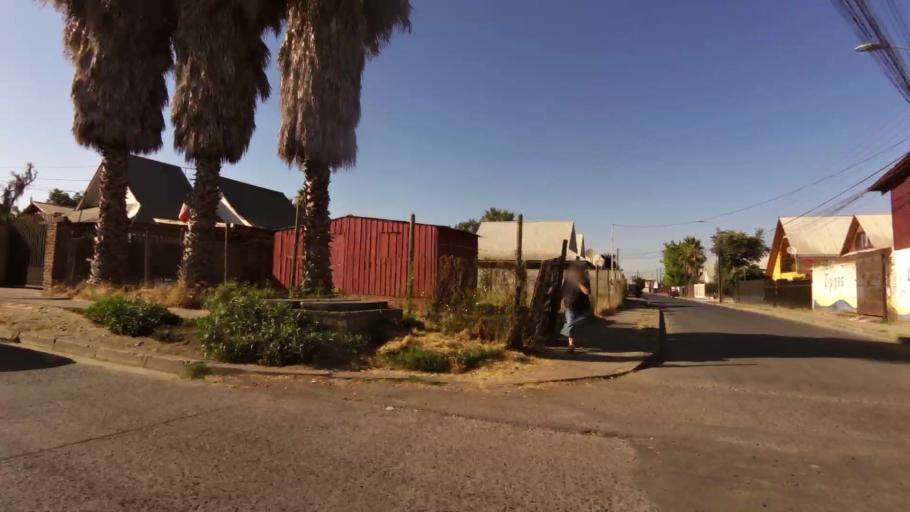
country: CL
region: Maule
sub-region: Provincia de Curico
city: Curico
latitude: -34.9870
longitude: -71.2544
